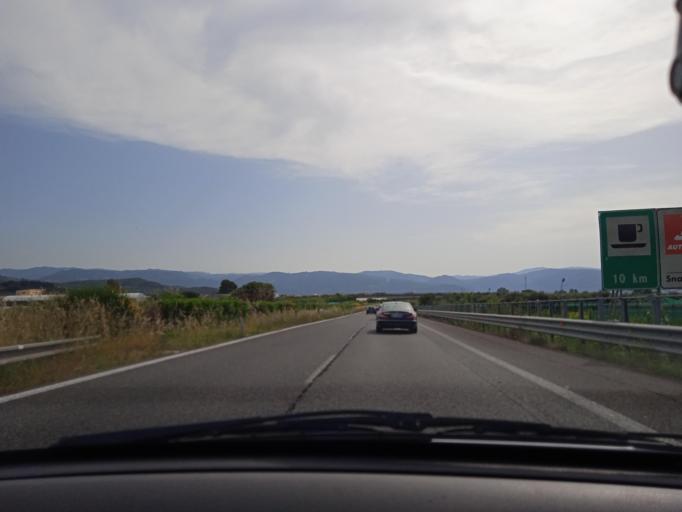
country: IT
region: Sicily
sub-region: Messina
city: Terme
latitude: 38.1368
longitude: 15.1495
